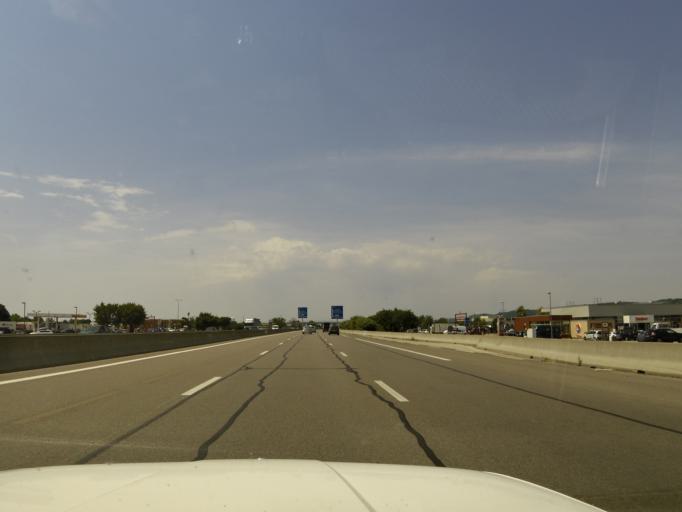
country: FR
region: Rhone-Alpes
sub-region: Departement de l'Ain
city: Dagneux
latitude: 45.8446
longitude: 5.0719
